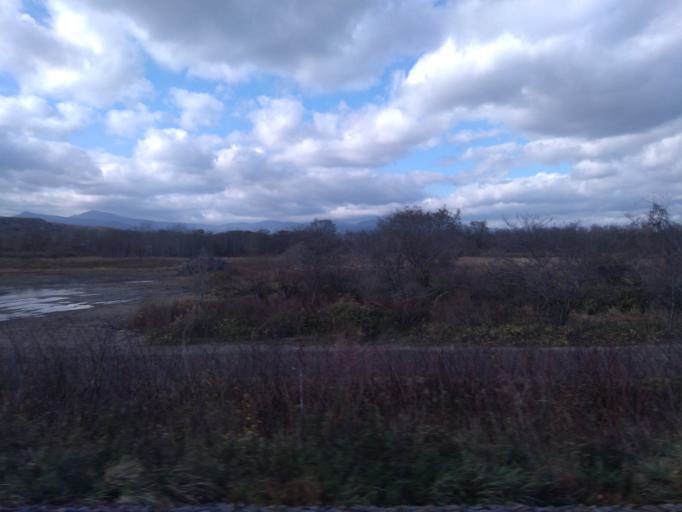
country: JP
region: Hokkaido
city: Shiraoi
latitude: 42.5023
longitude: 141.2755
